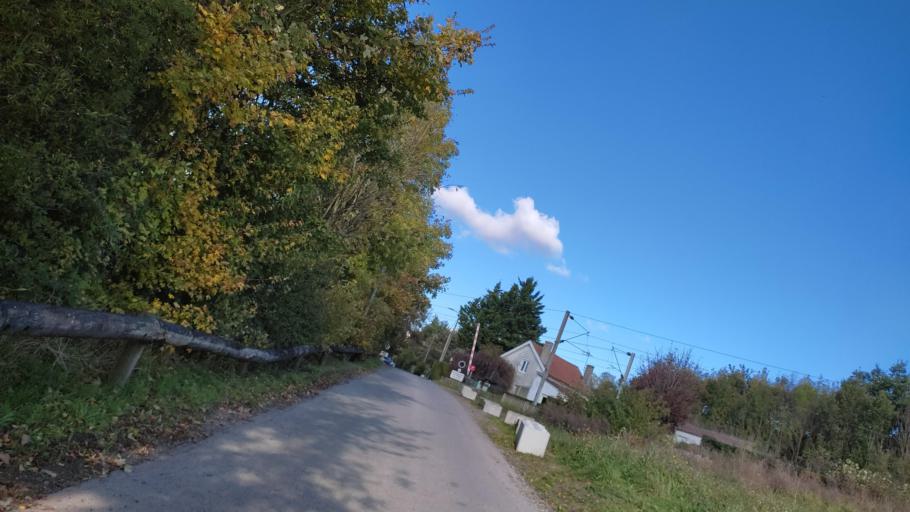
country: FR
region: Nord-Pas-de-Calais
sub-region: Departement du Pas-de-Calais
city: Saint-Laurent-Blangy
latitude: 50.3102
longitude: 2.8222
